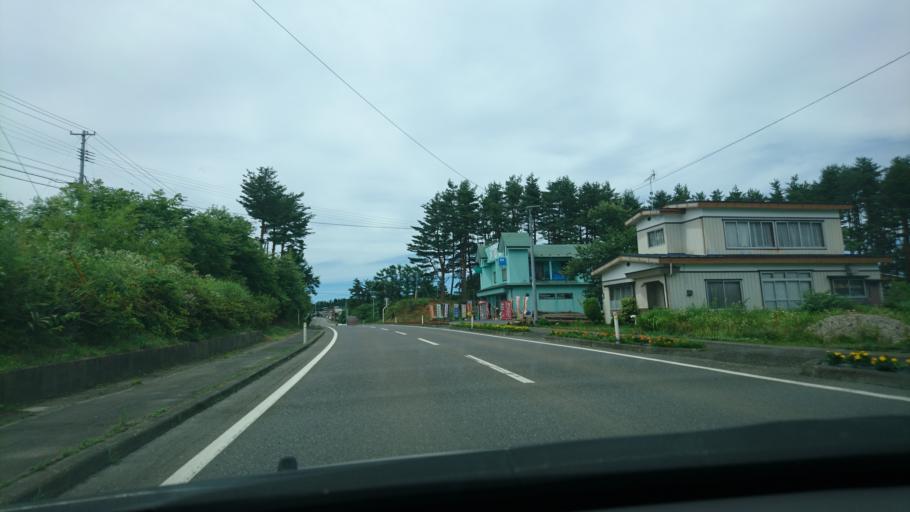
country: JP
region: Iwate
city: Miyako
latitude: 39.9205
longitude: 141.9029
